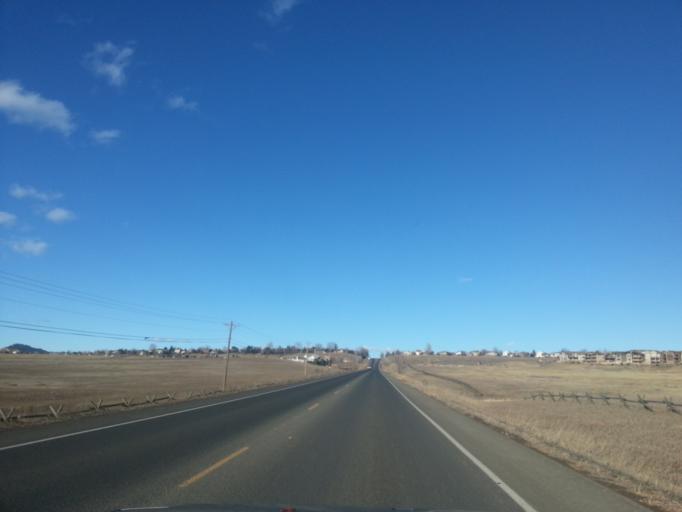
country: US
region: Colorado
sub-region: Larimer County
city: Fort Collins
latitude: 40.5179
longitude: -105.1151
